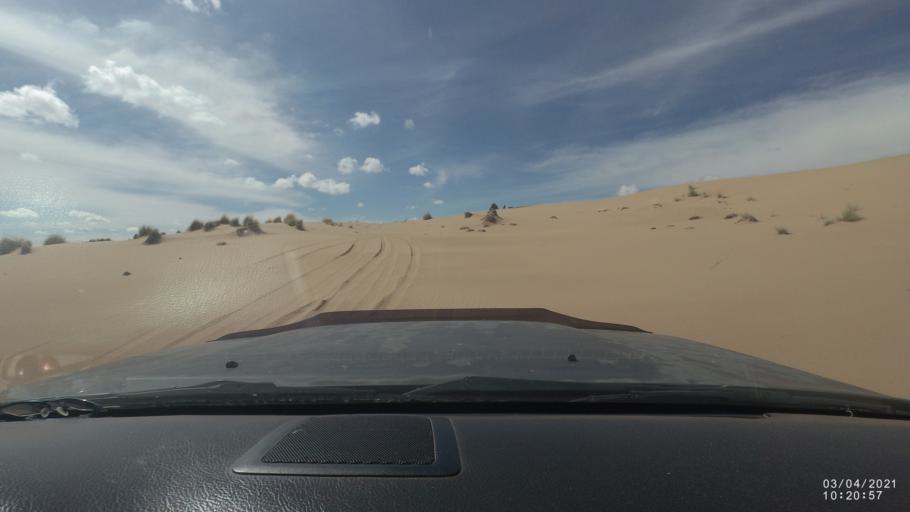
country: BO
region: Oruro
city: Poopo
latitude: -18.7057
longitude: -67.5242
